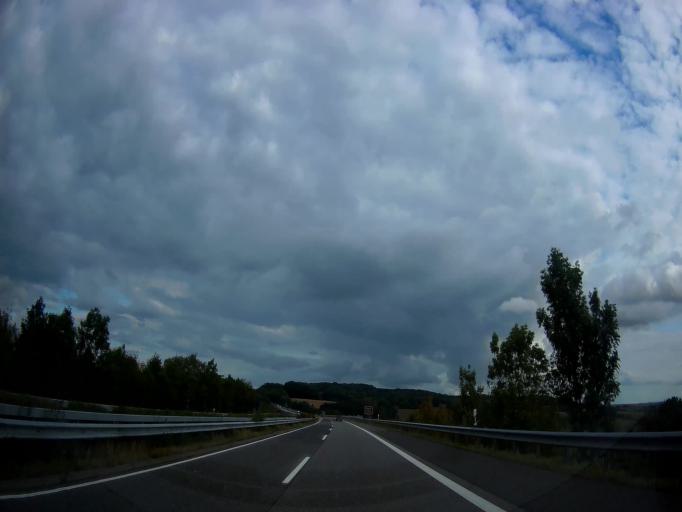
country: DE
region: Rheinland-Pfalz
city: Bickendorf
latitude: 50.0437
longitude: 6.5021
